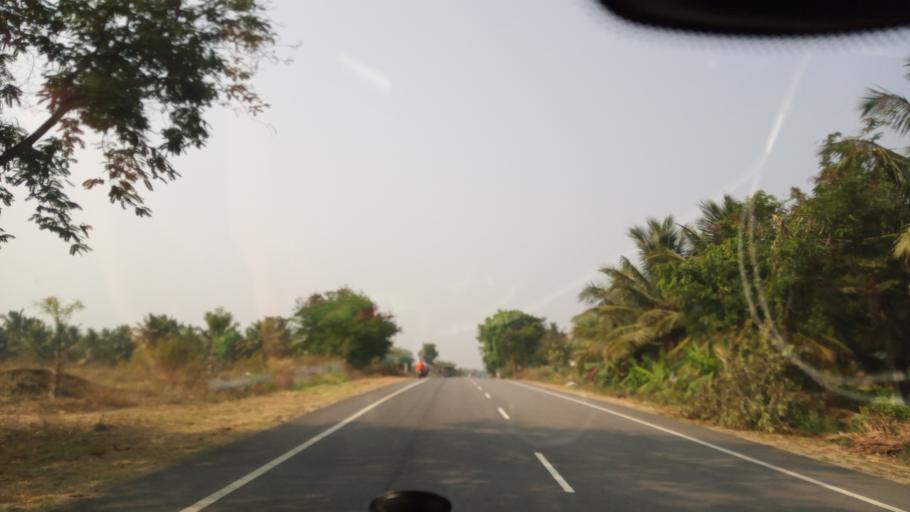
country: IN
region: Karnataka
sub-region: Mandya
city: Belluru
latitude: 12.9198
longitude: 76.7477
